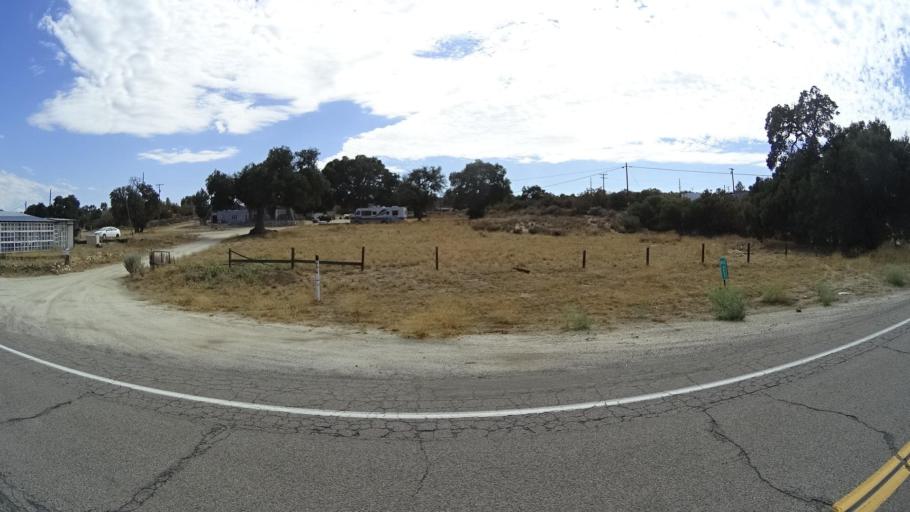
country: MX
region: Baja California
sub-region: Tecate
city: Cereso del Hongo
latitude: 32.6644
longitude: -116.2757
